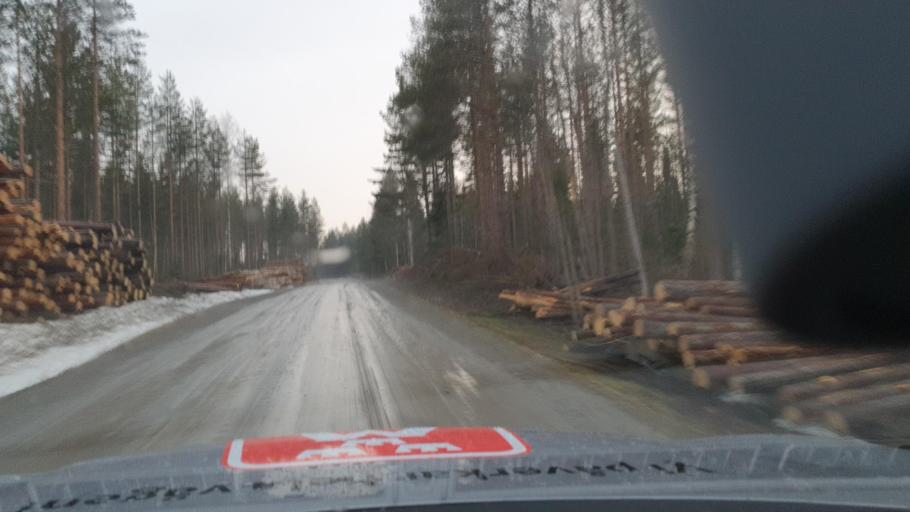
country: SE
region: Vaesternorrland
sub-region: OErnskoeldsviks Kommun
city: Bjasta
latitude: 63.2117
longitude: 18.3431
